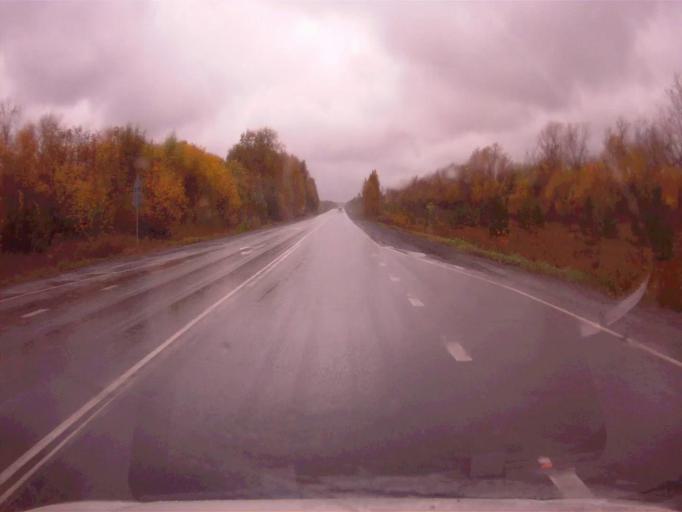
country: RU
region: Chelyabinsk
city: Argayash
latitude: 55.4351
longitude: 60.9783
